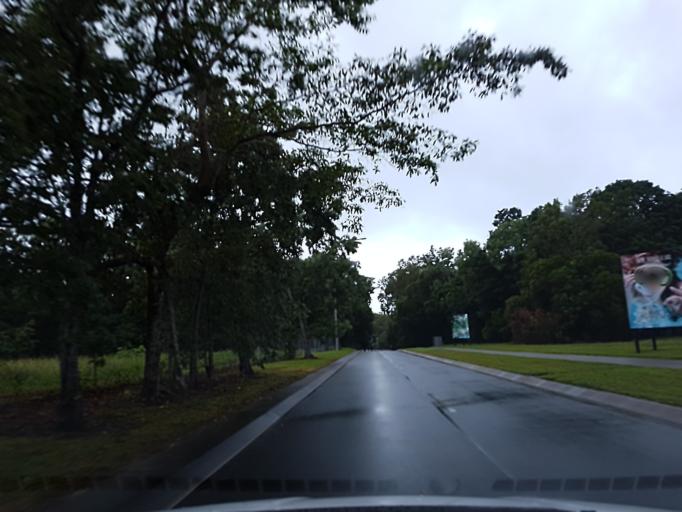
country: AU
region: Queensland
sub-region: Cairns
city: Palm Cove
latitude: -16.7523
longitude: 145.6682
